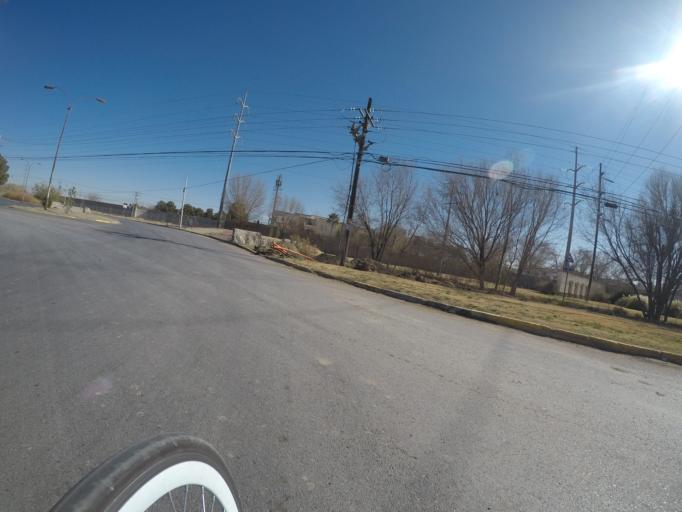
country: US
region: Texas
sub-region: El Paso County
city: Socorro
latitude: 31.7055
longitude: -106.3882
